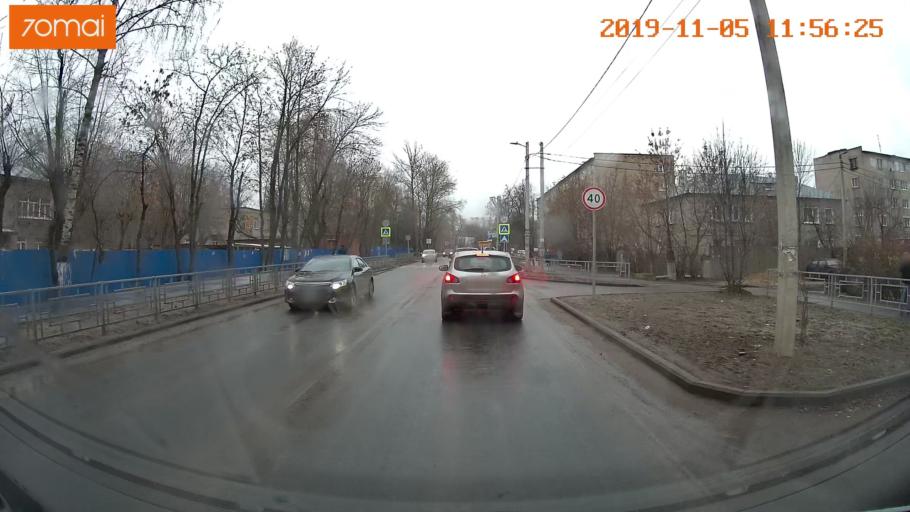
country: RU
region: Ivanovo
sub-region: Gorod Ivanovo
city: Ivanovo
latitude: 56.9861
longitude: 41.0306
